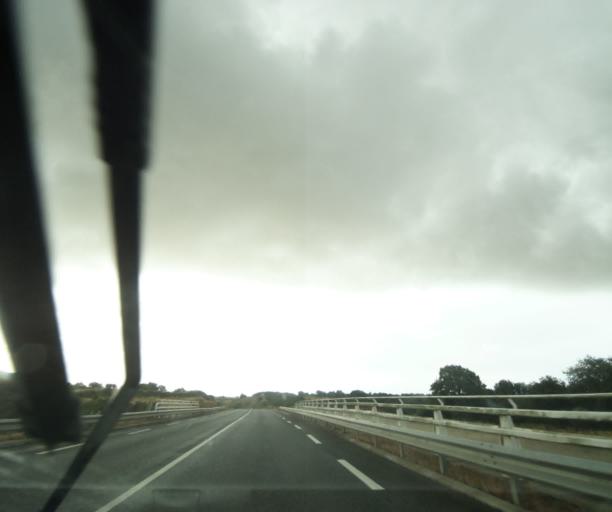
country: FR
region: Pays de la Loire
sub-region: Departement de la Vendee
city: Saint-Hilaire-de-Talmont
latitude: 46.4630
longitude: -1.6385
